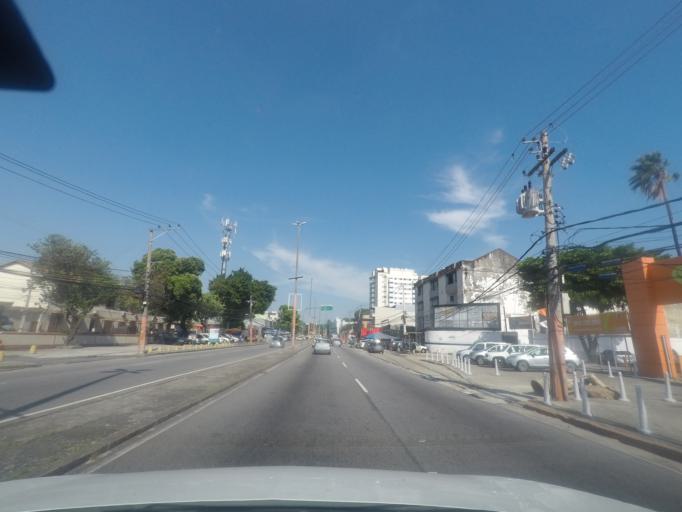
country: BR
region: Rio de Janeiro
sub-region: Sao Joao De Meriti
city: Sao Joao de Meriti
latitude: -22.8827
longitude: -43.3470
